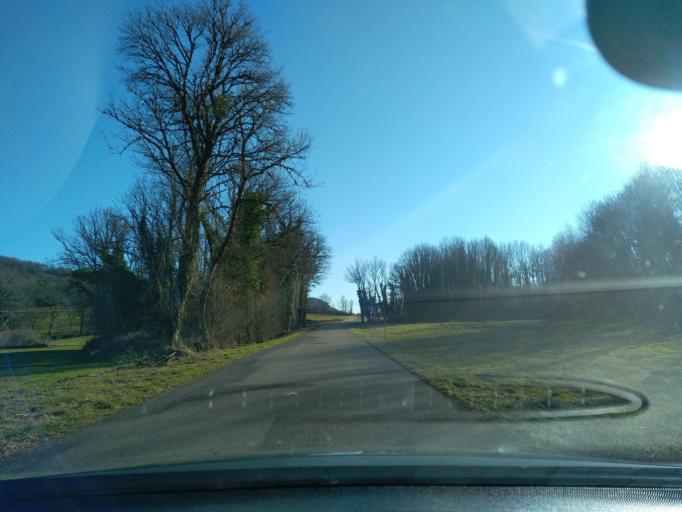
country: FR
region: Franche-Comte
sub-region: Departement du Jura
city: Poligny
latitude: 46.7150
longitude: 5.7386
